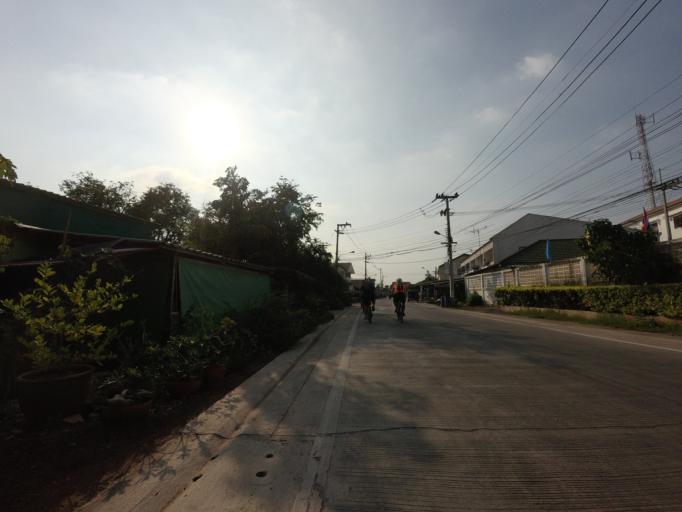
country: TH
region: Samut Sakhon
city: Samut Sakhon
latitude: 13.5139
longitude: 100.2892
